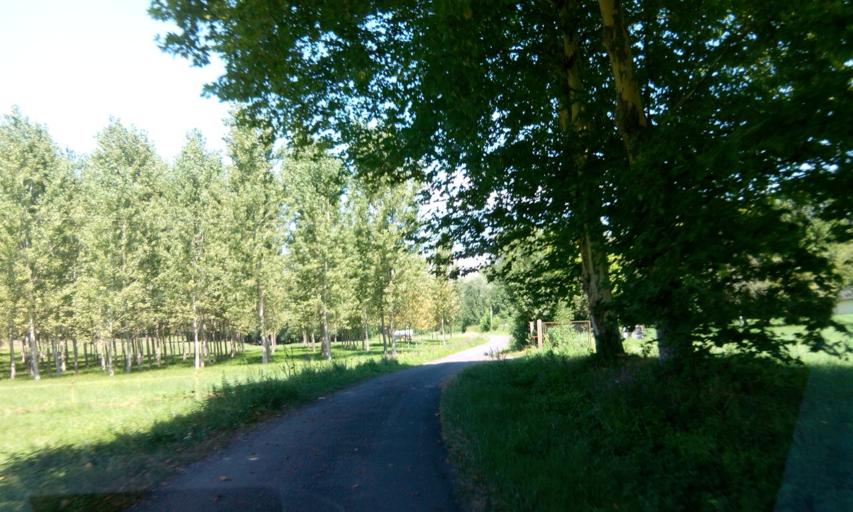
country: FR
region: Limousin
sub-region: Departement de la Correze
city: Meyssac
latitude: 45.0429
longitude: 1.5988
